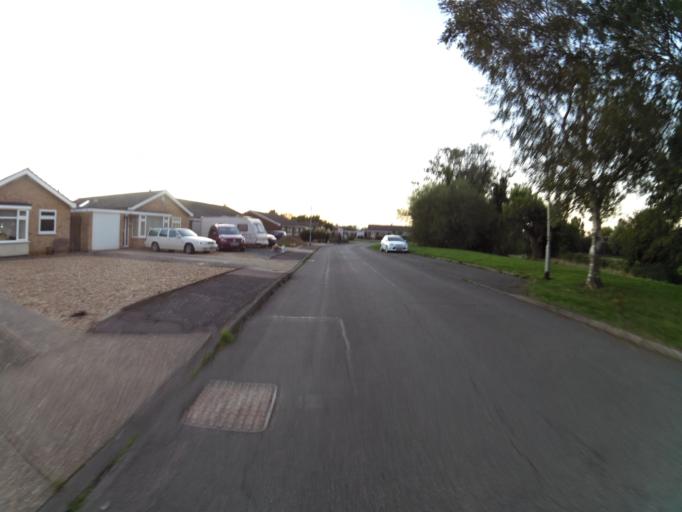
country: GB
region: England
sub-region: Suffolk
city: Bramford
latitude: 52.0805
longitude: 1.1003
